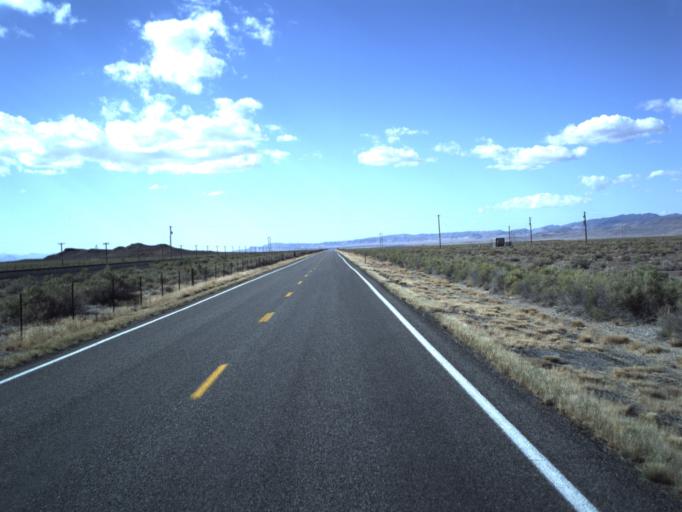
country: US
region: Utah
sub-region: Millard County
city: Delta
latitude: 39.1609
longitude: -112.7125
